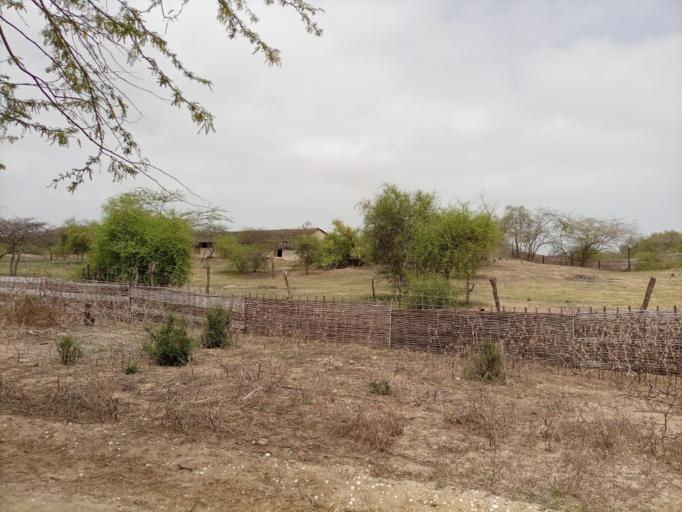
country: SN
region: Saint-Louis
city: Saint-Louis
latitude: 15.9281
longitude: -16.4681
